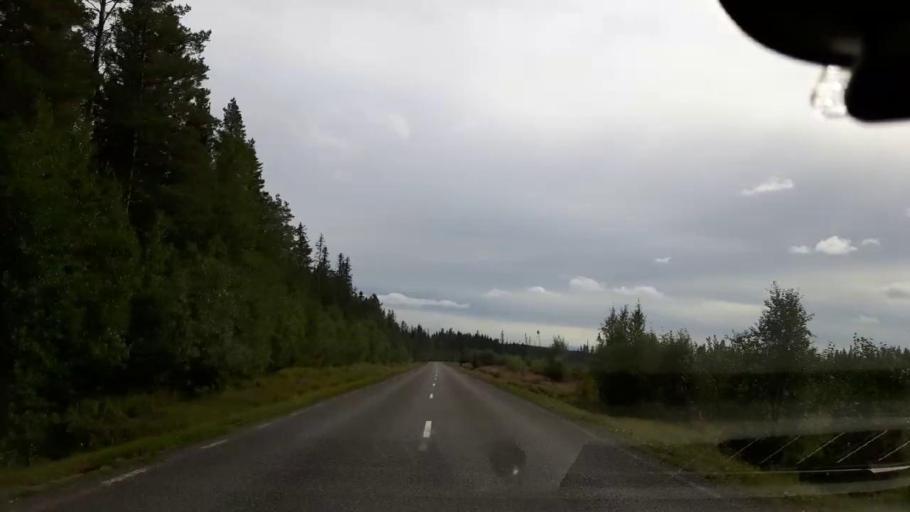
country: SE
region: Jaemtland
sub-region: Ragunda Kommun
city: Hammarstrand
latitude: 63.1300
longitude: 15.8867
